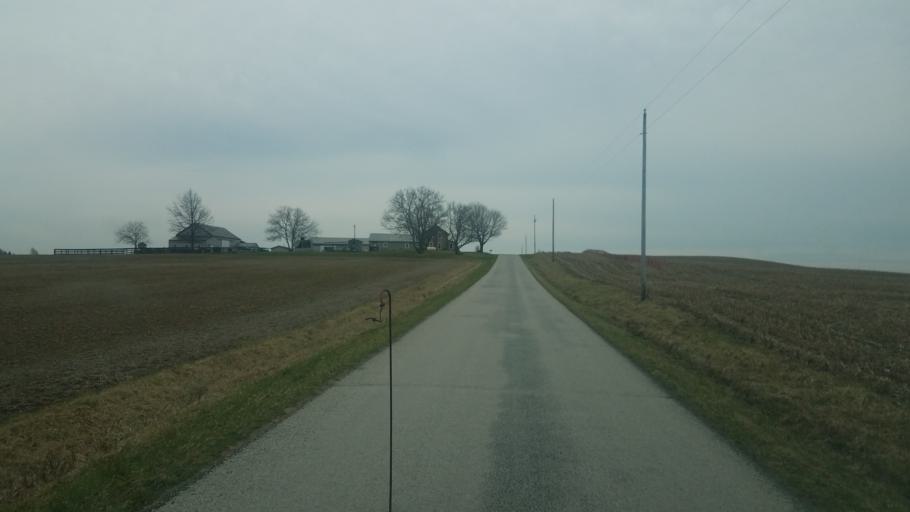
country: US
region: Ohio
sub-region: Huron County
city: Greenwich
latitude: 41.1110
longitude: -82.5639
